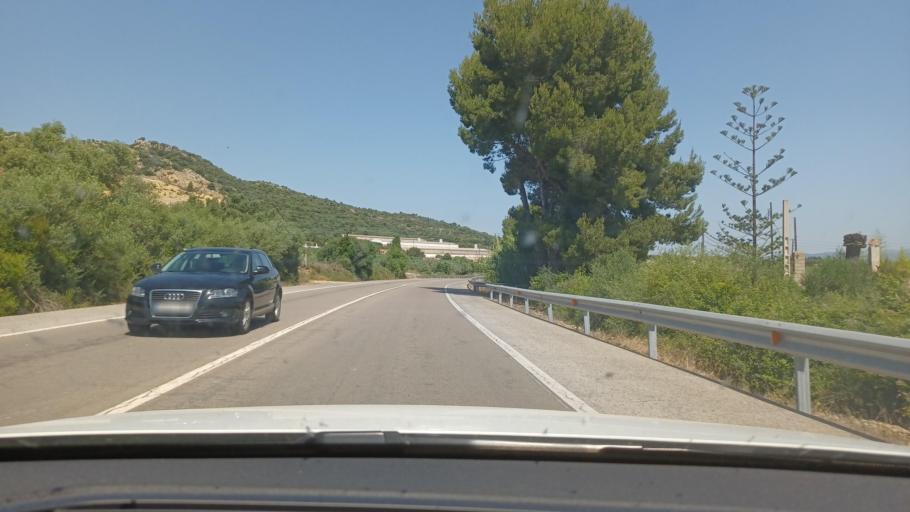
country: ES
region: Catalonia
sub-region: Provincia de Tarragona
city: Sant Carles de la Rapita
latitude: 40.6611
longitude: 0.5847
